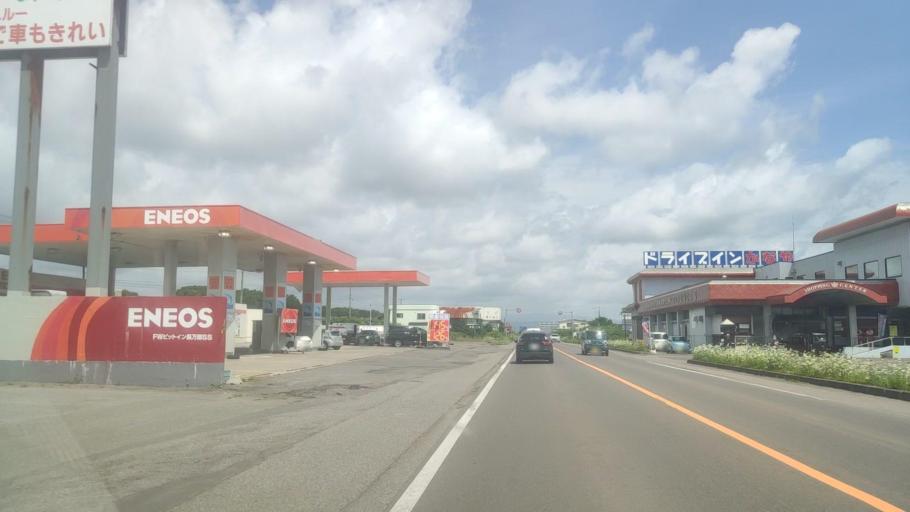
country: JP
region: Hokkaido
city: Niseko Town
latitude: 42.4924
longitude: 140.3595
